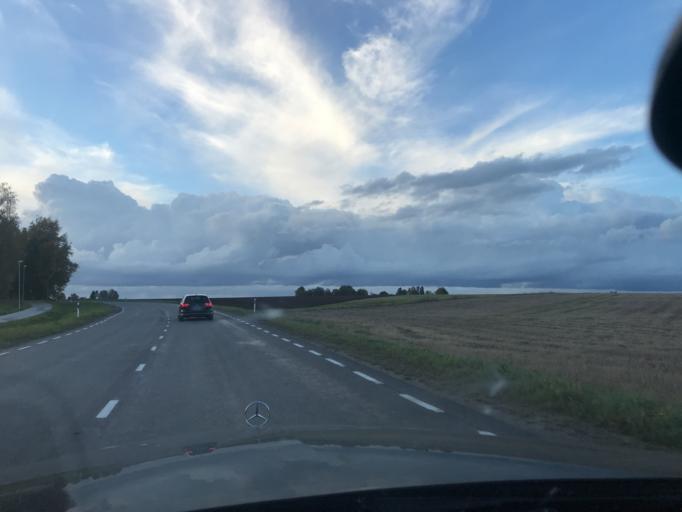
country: EE
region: Vorumaa
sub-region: Antsla vald
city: Vana-Antsla
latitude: 57.8938
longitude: 26.4985
